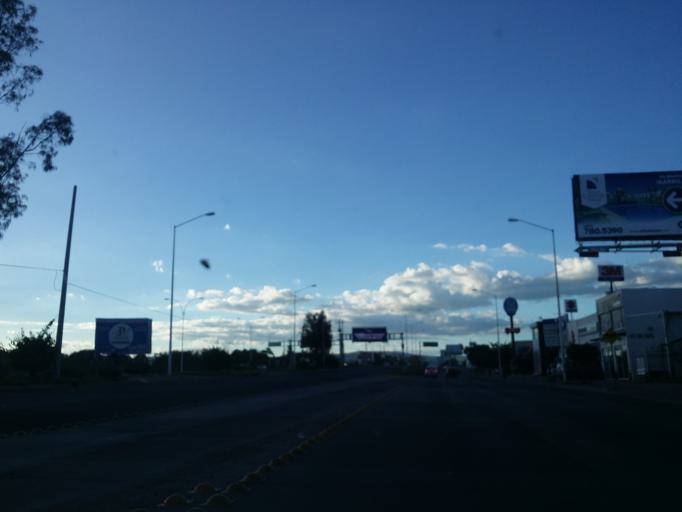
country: MX
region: Guanajuato
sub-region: Leon
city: Medina
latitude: 21.1663
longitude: -101.6518
